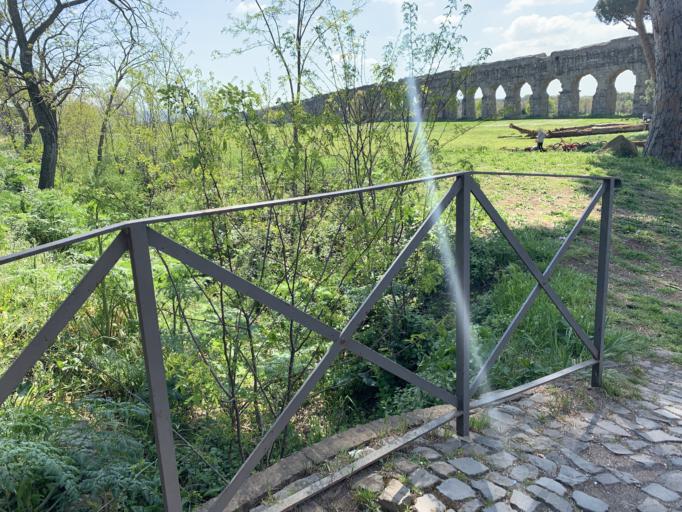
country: IT
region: Latium
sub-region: Citta metropolitana di Roma Capitale
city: Ciampino
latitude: 41.8471
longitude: 12.5615
